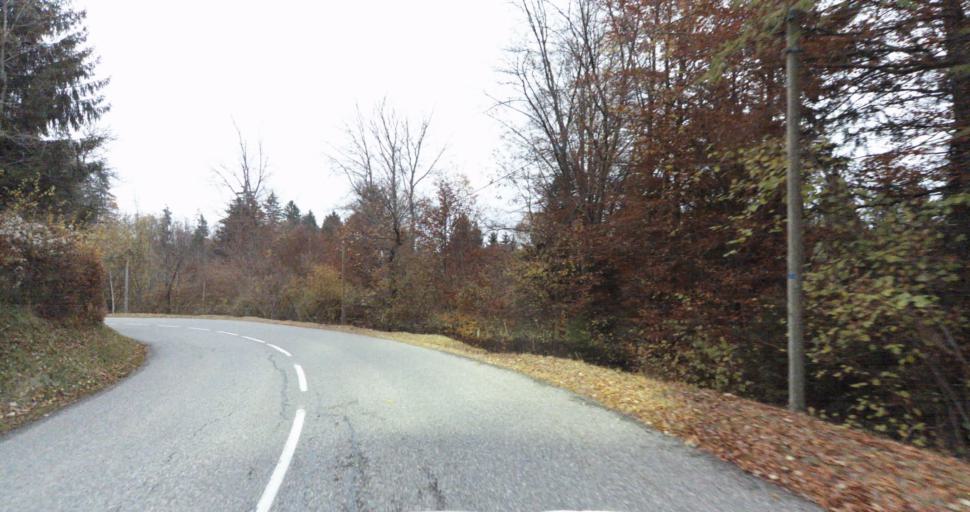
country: FR
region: Rhone-Alpes
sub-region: Departement de la Haute-Savoie
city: Saint-Jorioz
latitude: 45.7969
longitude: 6.1375
